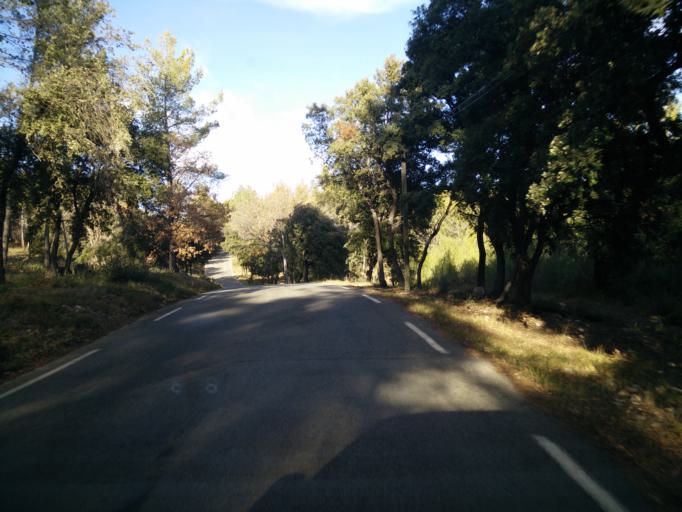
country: FR
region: Provence-Alpes-Cote d'Azur
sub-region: Departement du Var
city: Taradeau
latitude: 43.4702
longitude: 6.4320
